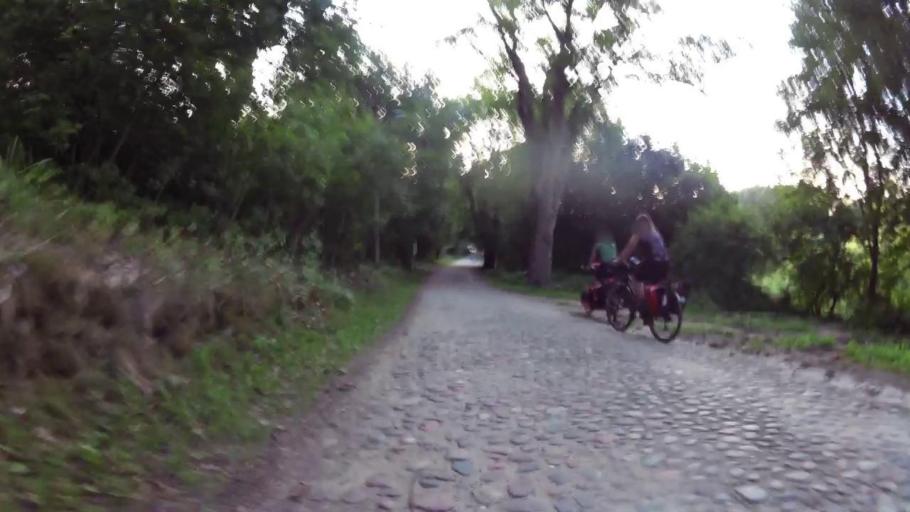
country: PL
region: West Pomeranian Voivodeship
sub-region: Powiat drawski
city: Drawsko Pomorskie
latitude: 53.4969
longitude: 15.7456
